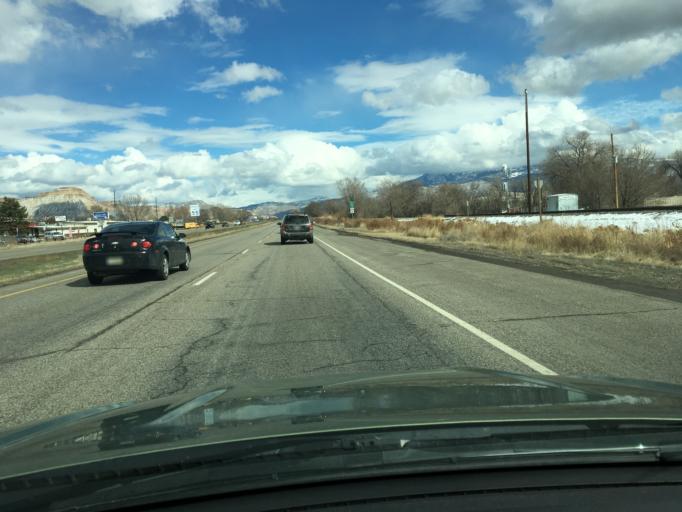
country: US
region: Colorado
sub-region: Mesa County
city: Fruitvale
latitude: 39.0781
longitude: -108.4919
